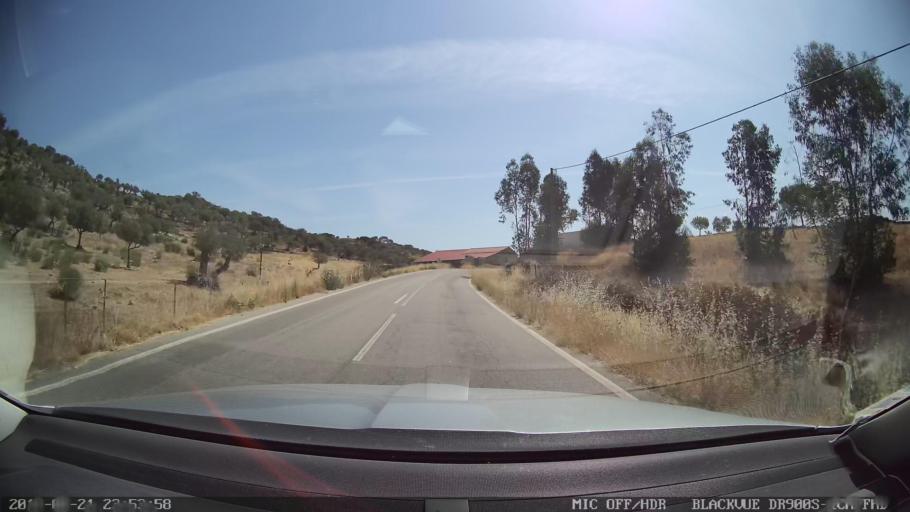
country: PT
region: Castelo Branco
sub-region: Idanha-A-Nova
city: Idanha-a-Nova
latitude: 39.9085
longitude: -7.2102
